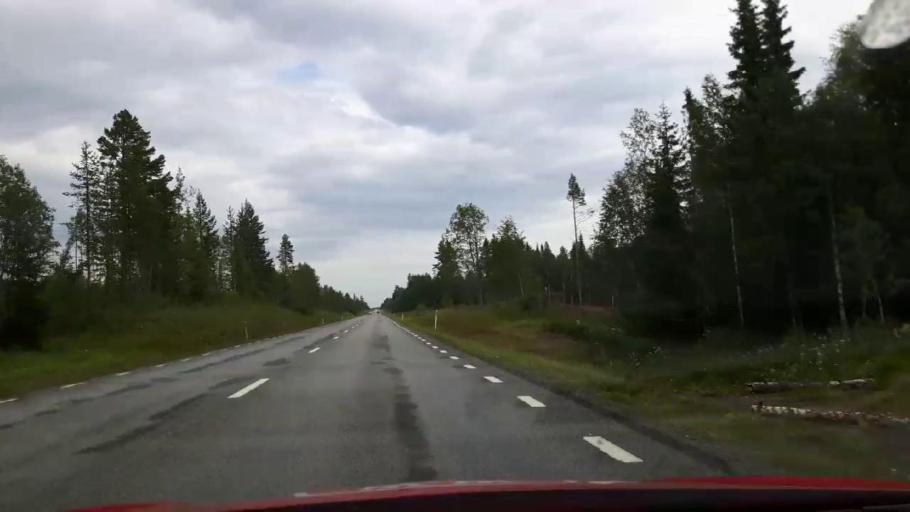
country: SE
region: Jaemtland
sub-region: Stroemsunds Kommun
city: Stroemsund
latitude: 63.6887
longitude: 15.4163
